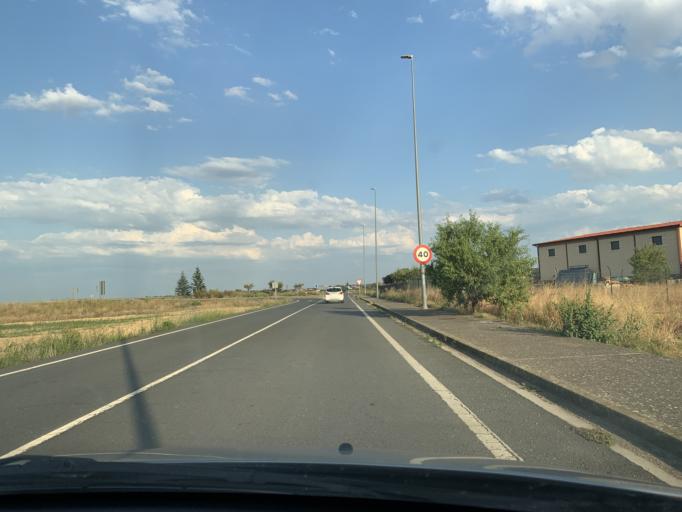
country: ES
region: La Rioja
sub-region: Provincia de La Rioja
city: Cuzcurrita de Rio Tiron
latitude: 42.5522
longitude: -2.9643
